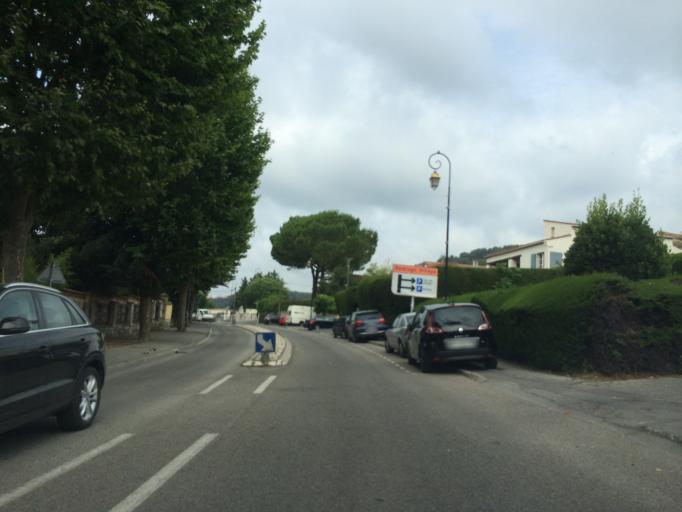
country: FR
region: Provence-Alpes-Cote d'Azur
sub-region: Departement des Alpes-Maritimes
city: La Colle-sur-Loup
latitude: 43.6862
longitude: 7.1044
